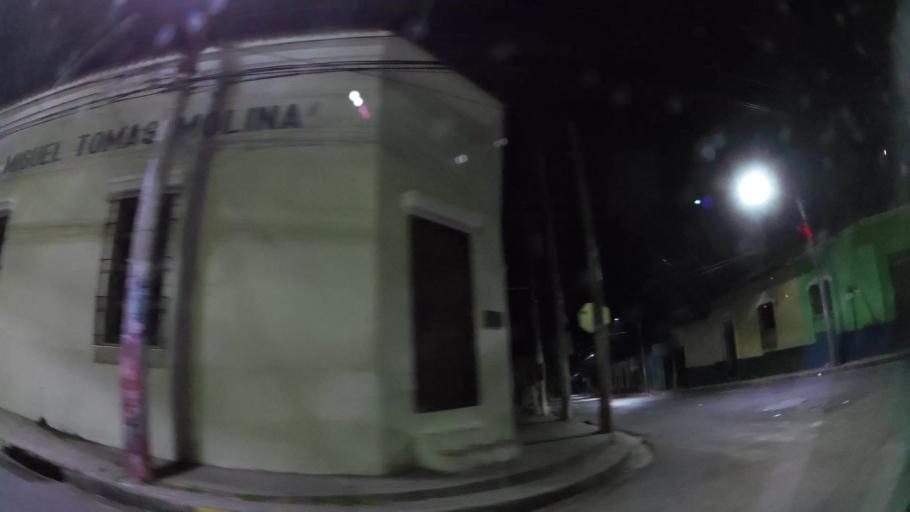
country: SV
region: La Paz
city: Zacatecoluca
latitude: 13.5084
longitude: -88.8674
